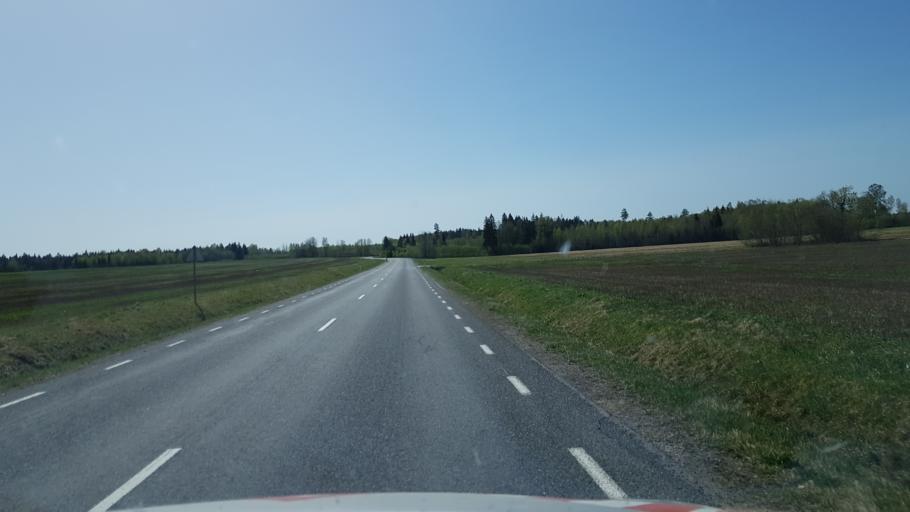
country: EE
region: Viljandimaa
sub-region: Suure-Jaani vald
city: Suure-Jaani
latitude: 58.4946
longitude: 25.4511
